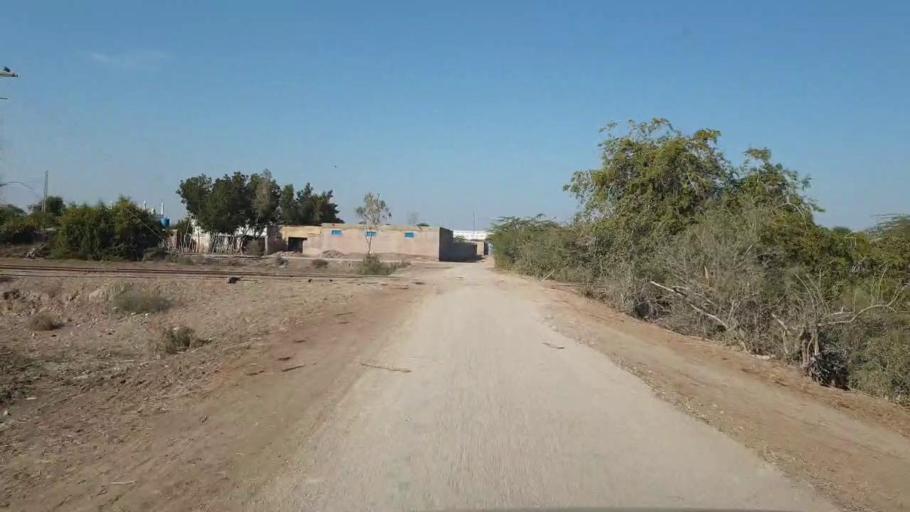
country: PK
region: Sindh
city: Shahpur Chakar
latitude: 26.1552
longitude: 68.6839
